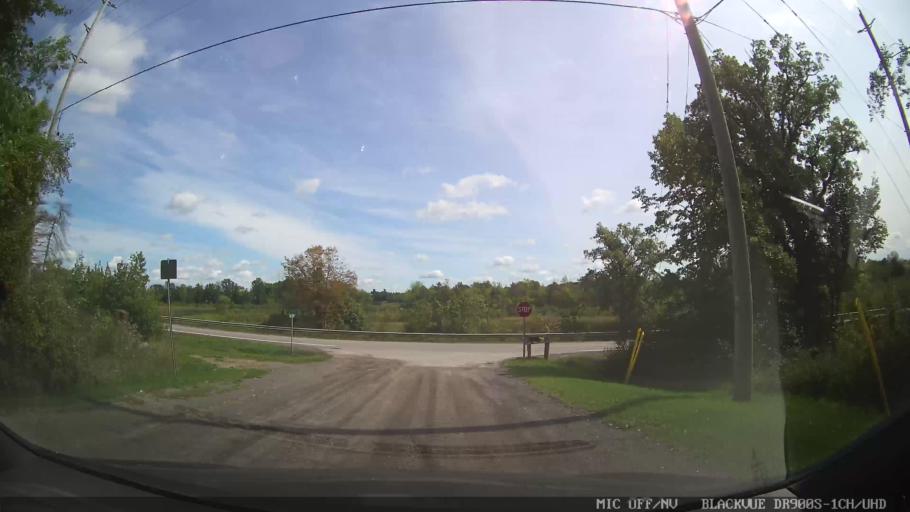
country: CA
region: Ontario
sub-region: Lanark County
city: Smiths Falls
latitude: 44.9667
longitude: -75.8255
